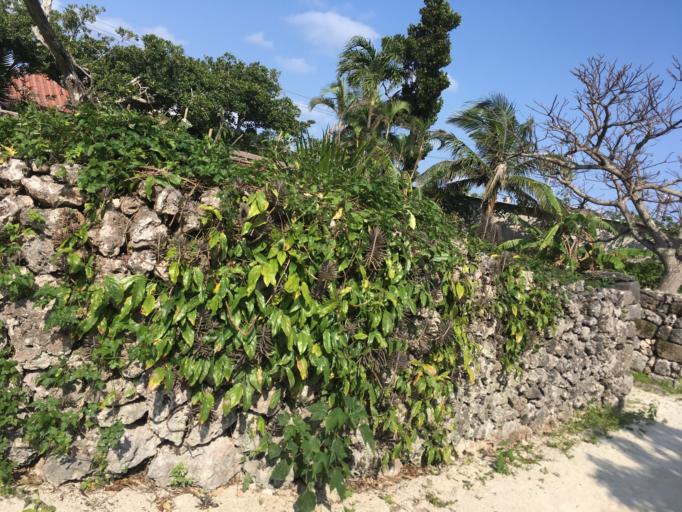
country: JP
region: Okinawa
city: Ishigaki
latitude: 24.3299
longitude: 124.0868
